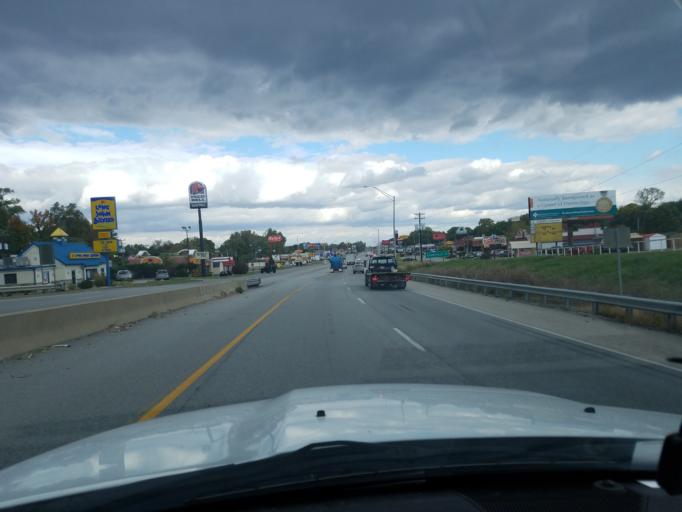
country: US
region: Kentucky
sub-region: Henderson County
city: Henderson
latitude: 37.8612
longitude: -87.5754
